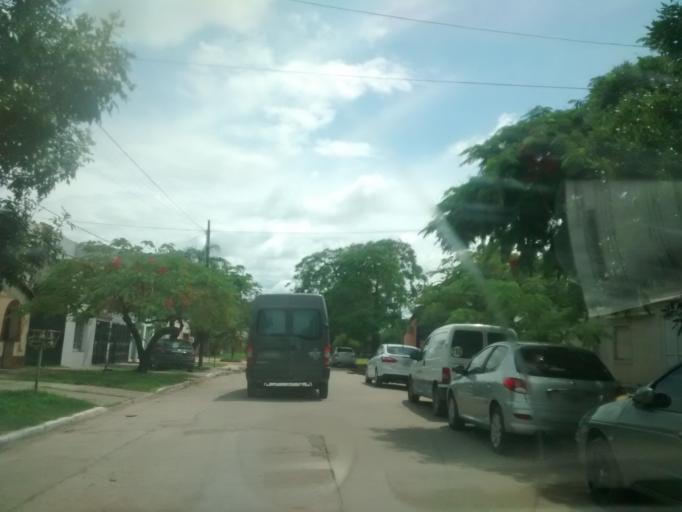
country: AR
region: Chaco
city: Resistencia
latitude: -27.4461
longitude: -58.9986
